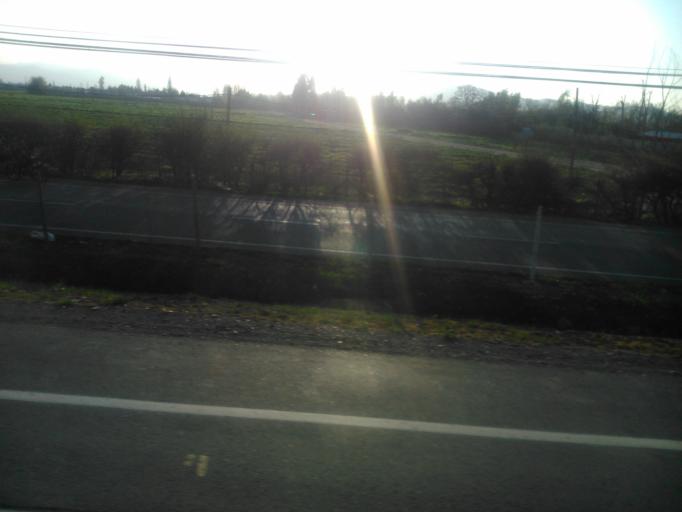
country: CL
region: Santiago Metropolitan
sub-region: Provincia de Maipo
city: Buin
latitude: -33.7456
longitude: -70.7388
